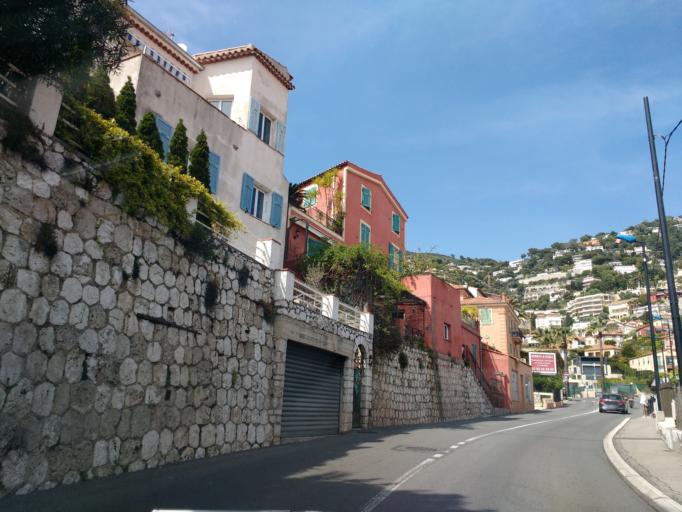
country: FR
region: Provence-Alpes-Cote d'Azur
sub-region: Departement des Alpes-Maritimes
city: Villefranche-sur-Mer
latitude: 43.7049
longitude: 7.3095
